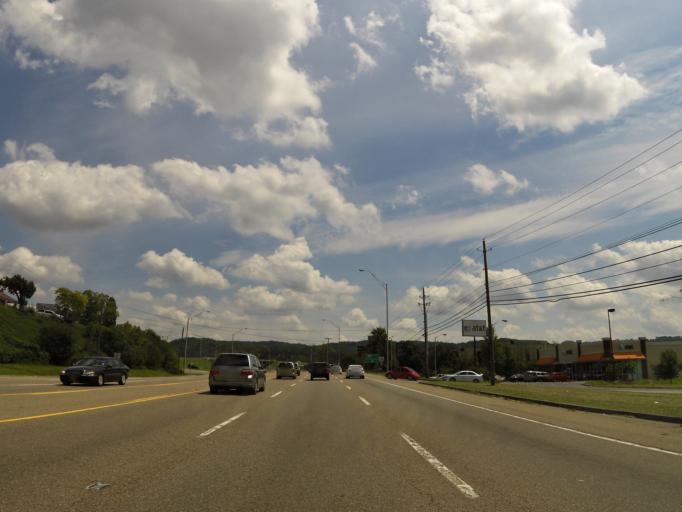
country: US
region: Tennessee
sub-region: Sullivan County
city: Bloomingdale
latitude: 36.5457
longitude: -82.5129
